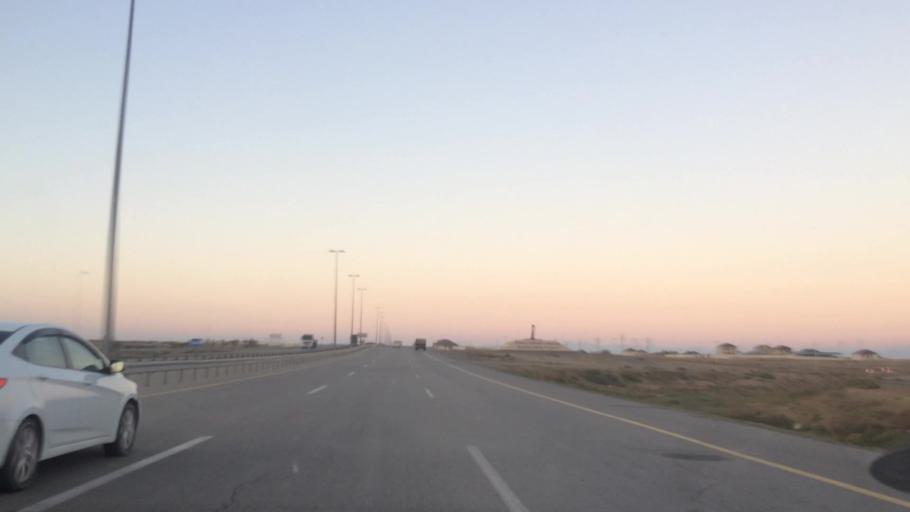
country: AZ
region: Baki
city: Qobustan
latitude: 39.9798
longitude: 49.4221
